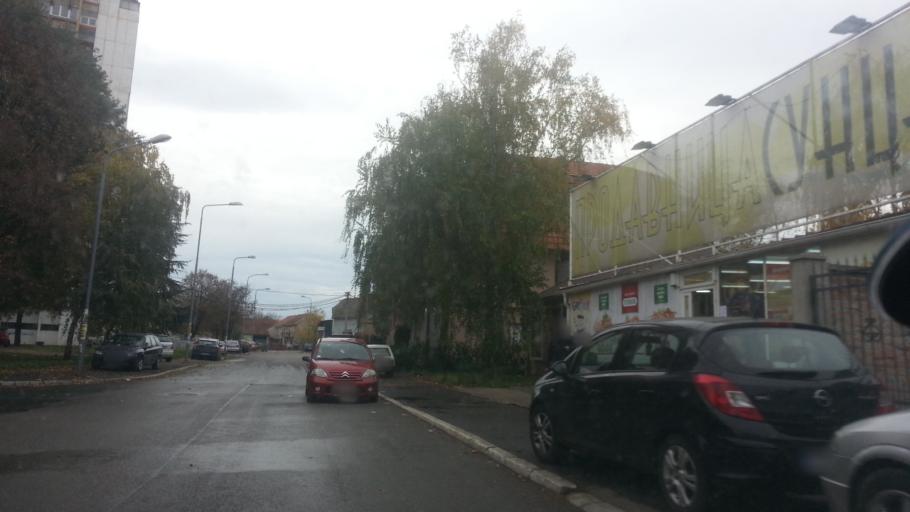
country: RS
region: Central Serbia
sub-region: Belgrade
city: Zemun
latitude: 44.8433
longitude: 20.3889
